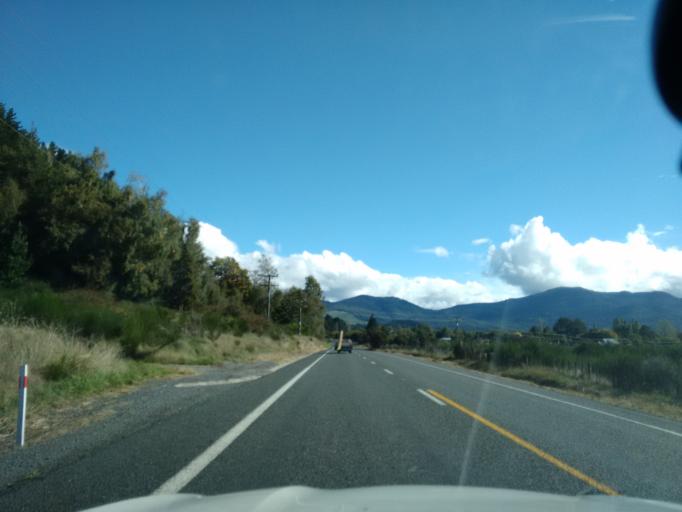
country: NZ
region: Waikato
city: Turangi
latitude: -38.9810
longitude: 175.8241
